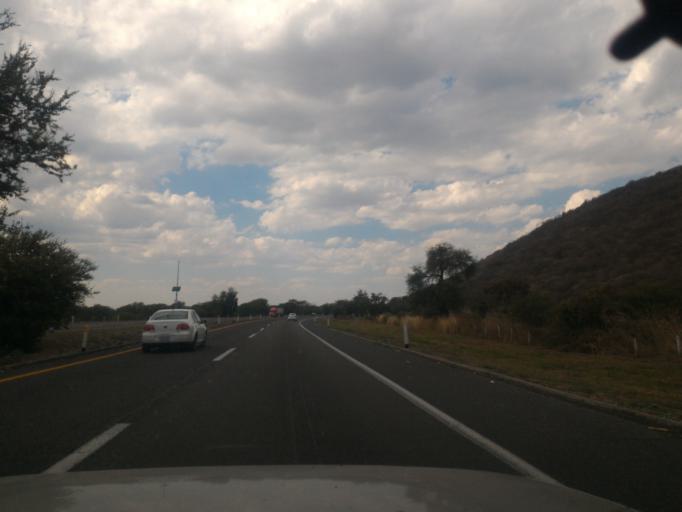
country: MX
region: Jalisco
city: Zacoalco de Torres
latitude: 20.1906
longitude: -103.5202
